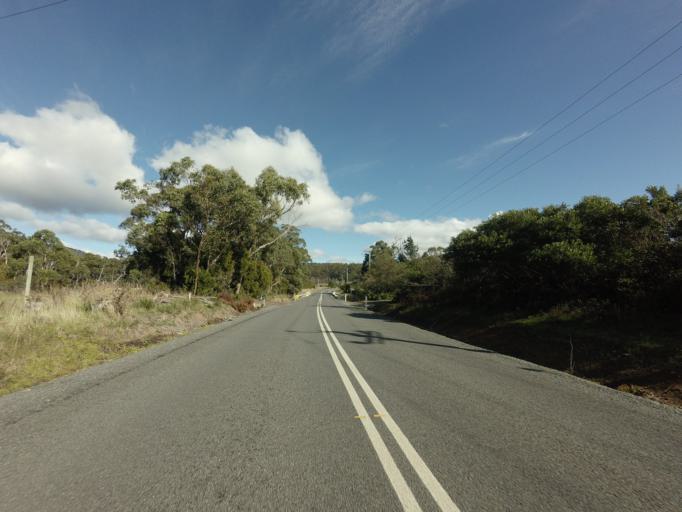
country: AU
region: Tasmania
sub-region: Clarence
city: Sandford
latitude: -43.0641
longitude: 147.8400
